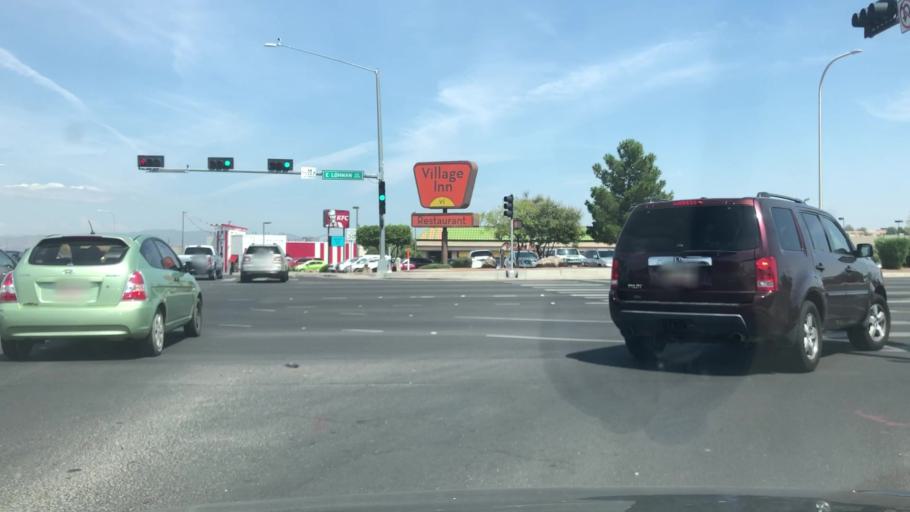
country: US
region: New Mexico
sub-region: Dona Ana County
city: University Park
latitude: 32.3151
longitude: -106.7444
